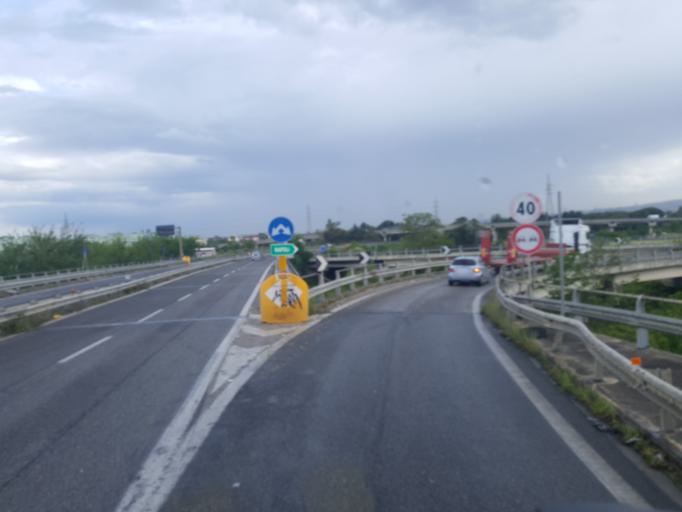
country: IT
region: Campania
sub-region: Provincia di Napoli
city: Pascarola
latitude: 40.9725
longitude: 14.2931
